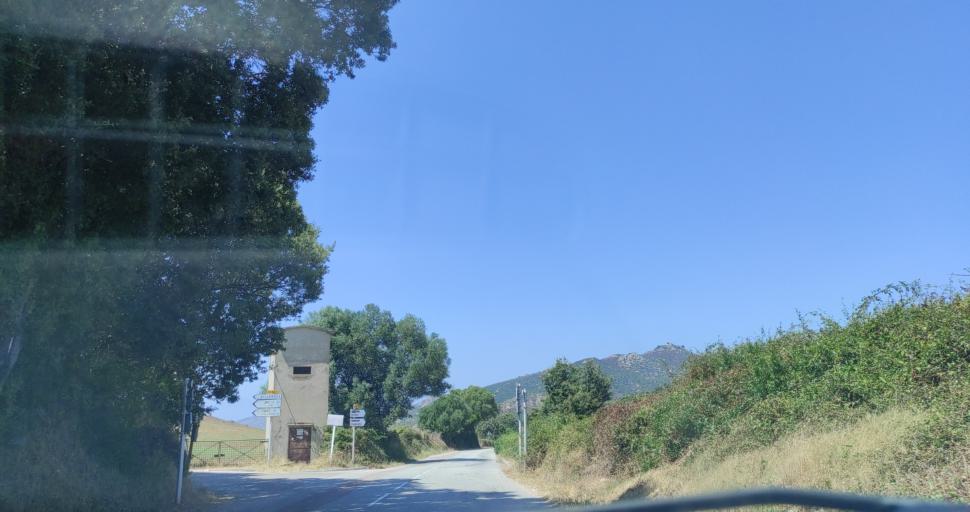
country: FR
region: Corsica
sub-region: Departement de la Corse-du-Sud
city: Alata
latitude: 41.9661
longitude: 8.7191
